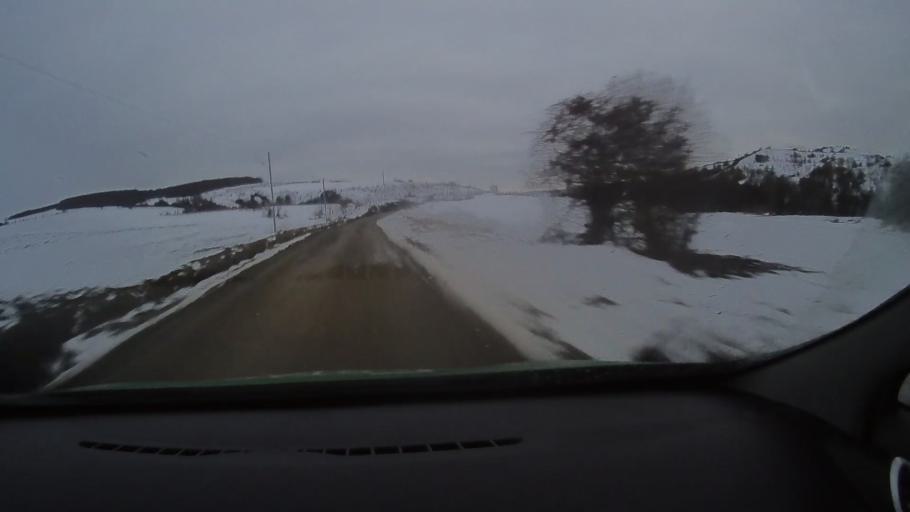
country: RO
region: Harghita
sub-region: Comuna Darjiu
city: Darjiu
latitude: 46.2069
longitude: 25.2434
